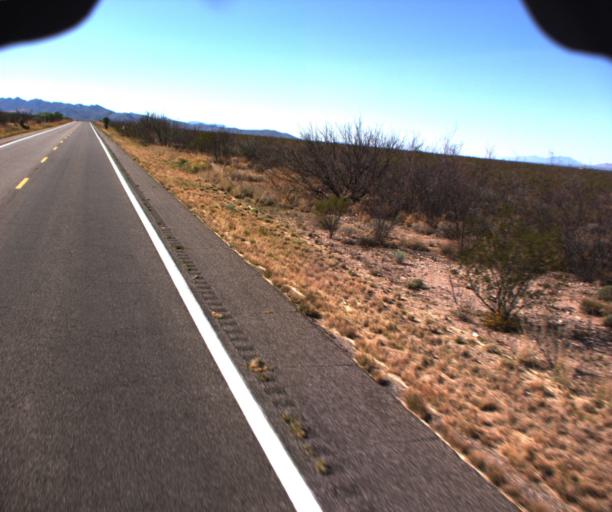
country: US
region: Arizona
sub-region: Cochise County
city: Tombstone
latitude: 31.6069
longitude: -110.0494
